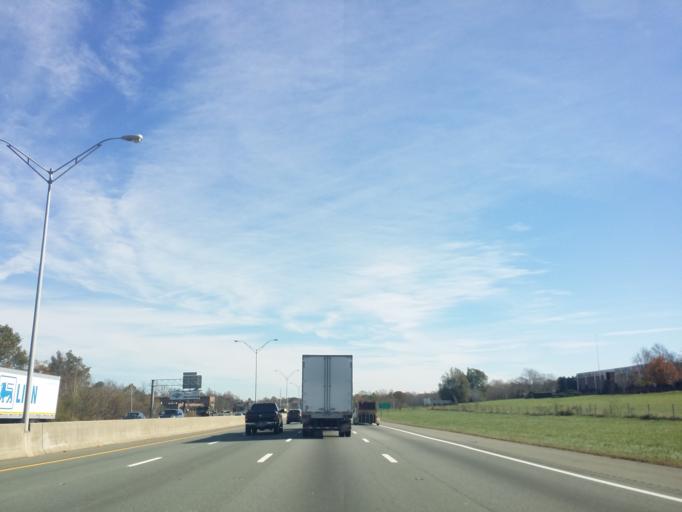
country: US
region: North Carolina
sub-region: Alamance County
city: Burlington
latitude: 36.0649
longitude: -79.4495
